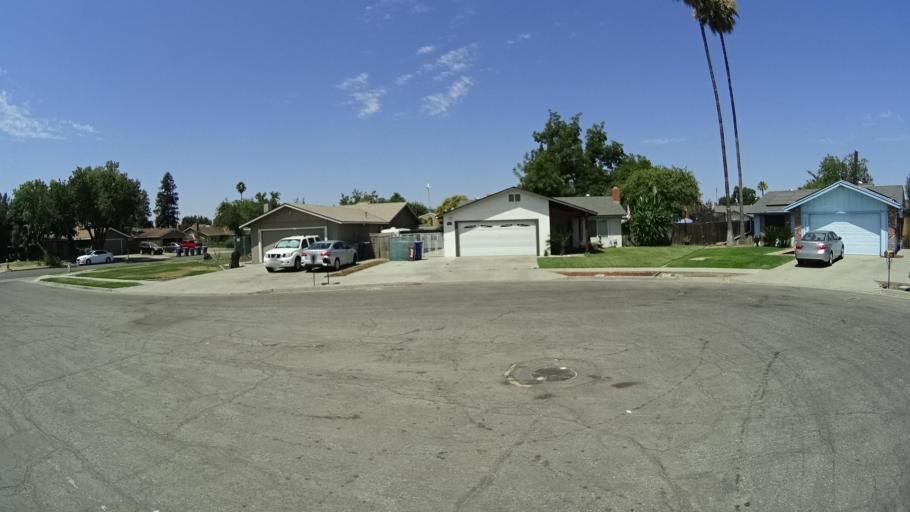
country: US
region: California
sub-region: Fresno County
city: Tarpey Village
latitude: 36.7859
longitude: -119.6842
